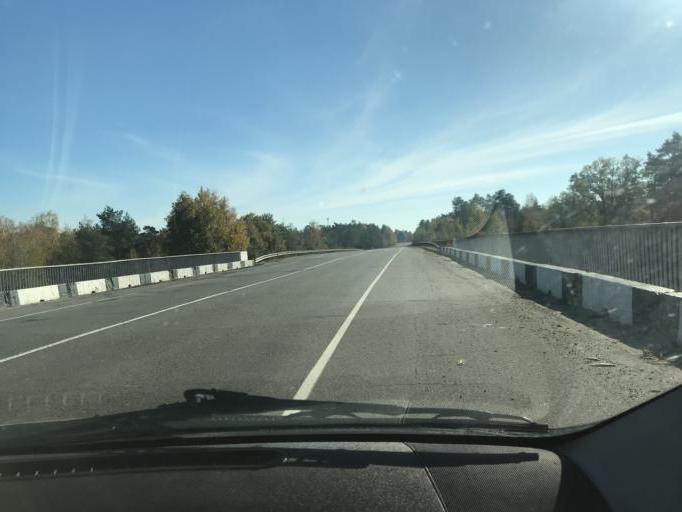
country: BY
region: Brest
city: Mikashevichy
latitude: 52.2438
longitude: 27.4444
